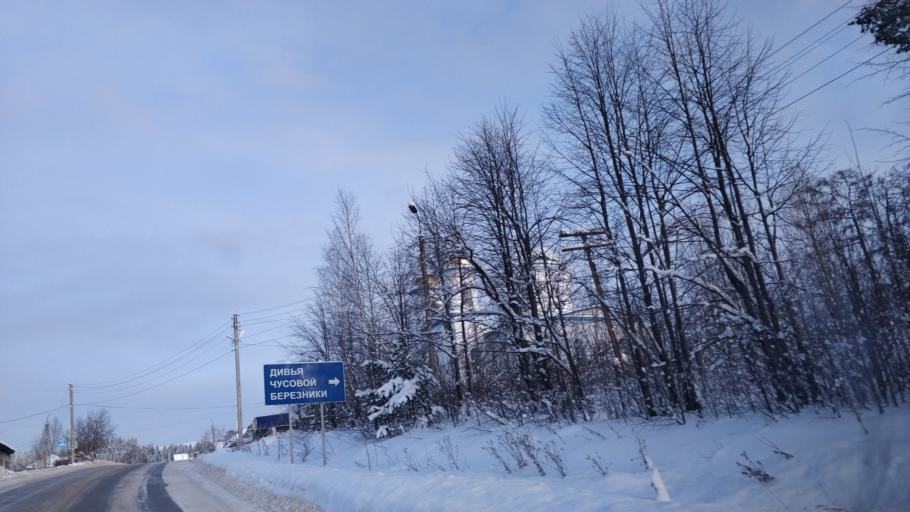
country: RU
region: Perm
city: Polazna
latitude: 58.3069
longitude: 56.4198
